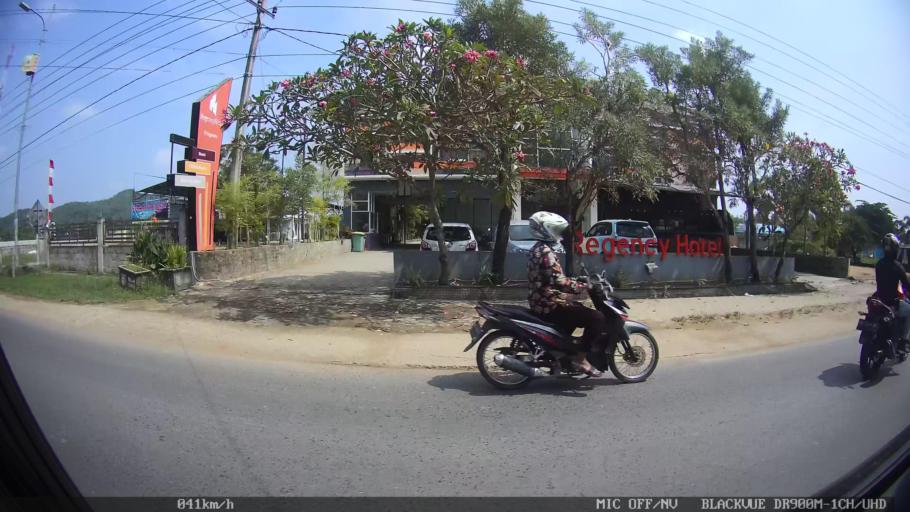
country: ID
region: Lampung
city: Gadingrejo
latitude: -5.3828
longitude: 105.0197
